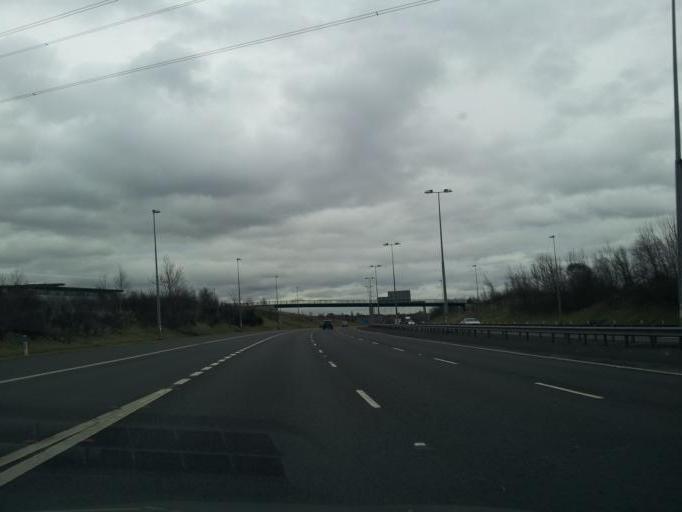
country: GB
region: England
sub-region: Staffordshire
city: Great Wyrley
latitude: 52.6723
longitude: -2.0131
